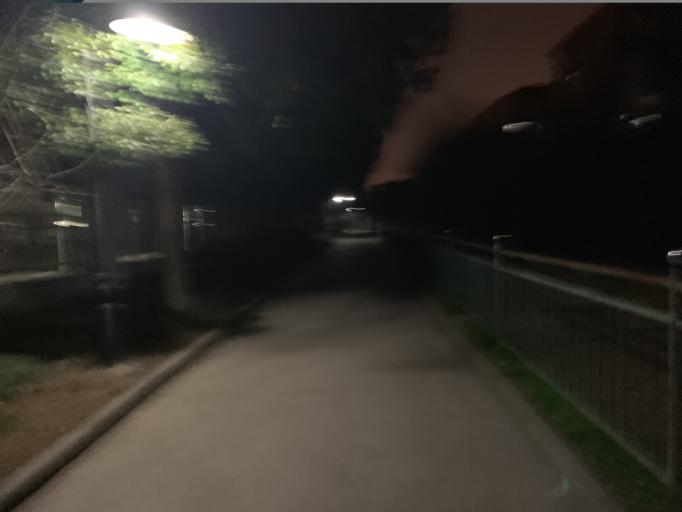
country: CN
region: Shanghai Shi
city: Changqiao
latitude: 31.1460
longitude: 121.4285
